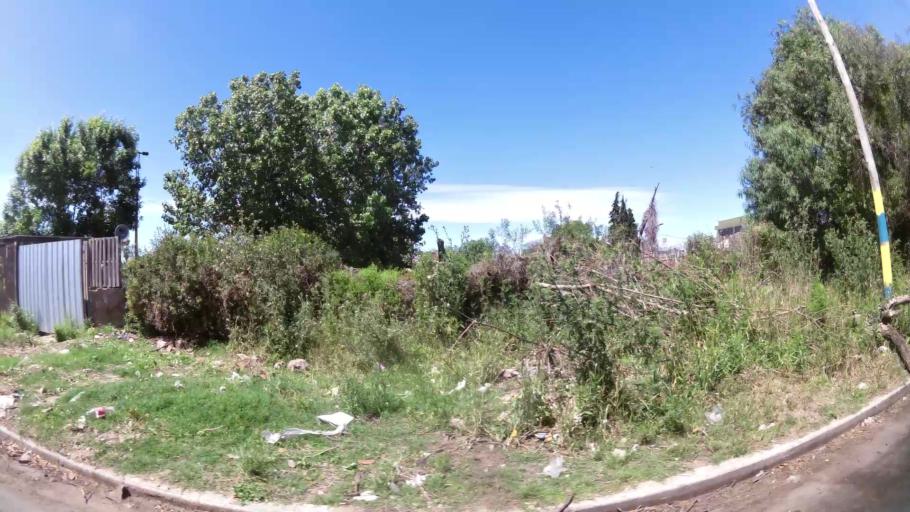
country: AR
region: Santa Fe
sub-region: Departamento de Rosario
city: Rosario
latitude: -32.9557
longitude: -60.7080
